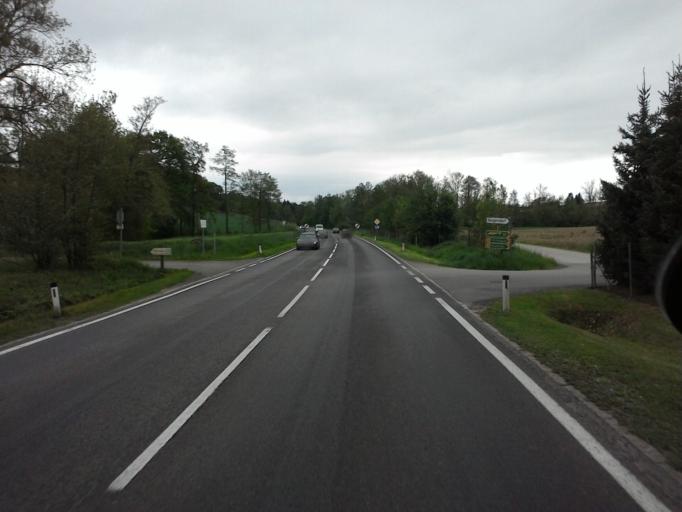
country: AT
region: Upper Austria
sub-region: Wels-Land
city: Thalheim bei Wels
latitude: 48.1366
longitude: 14.0475
